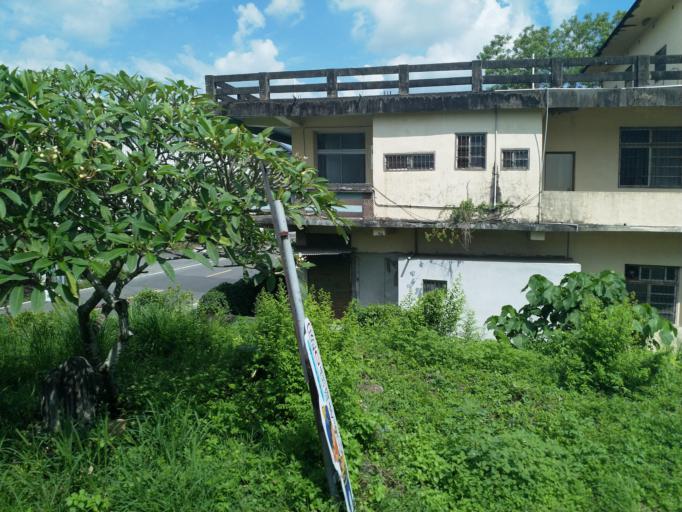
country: TW
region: Taiwan
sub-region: Pingtung
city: Pingtung
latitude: 22.8793
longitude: 120.5690
